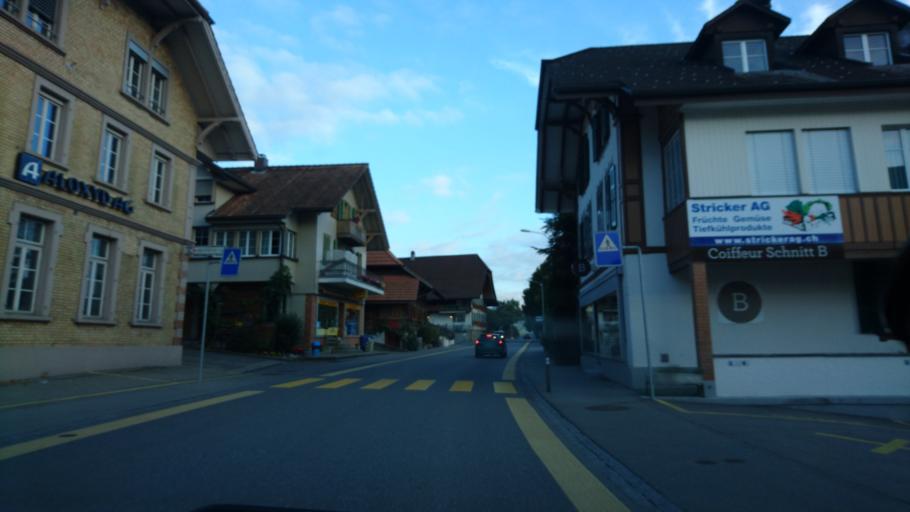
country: CH
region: Bern
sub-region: Bern-Mittelland District
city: Zaziwil
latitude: 46.9056
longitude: 7.6419
